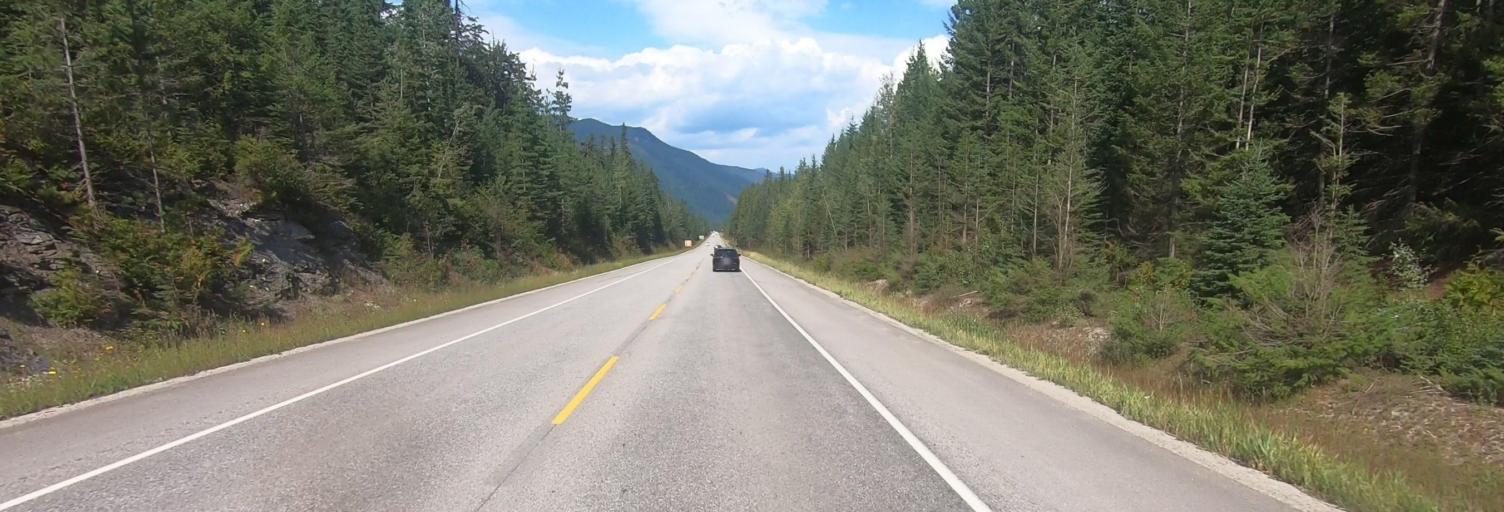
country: CA
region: British Columbia
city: Golden
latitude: 51.4962
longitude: -117.4027
